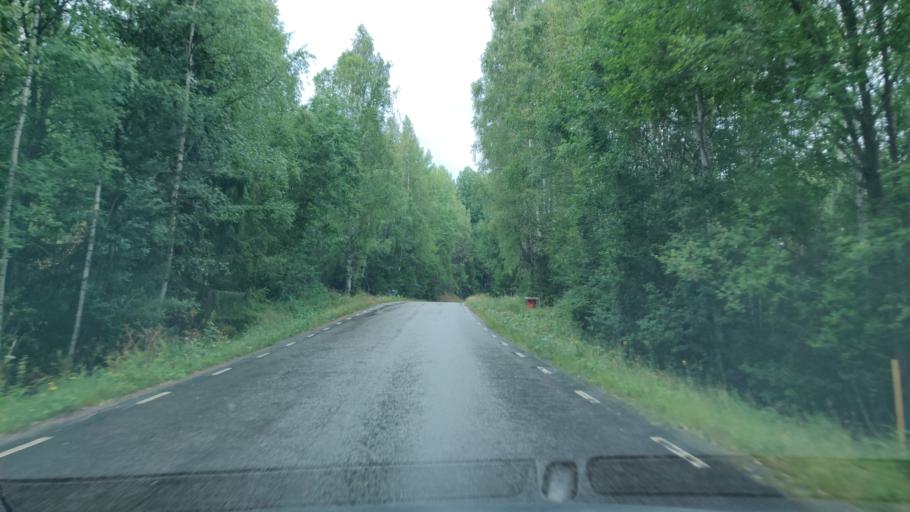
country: SE
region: Vaermland
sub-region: Munkfors Kommun
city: Munkfors
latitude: 59.8473
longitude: 13.5331
